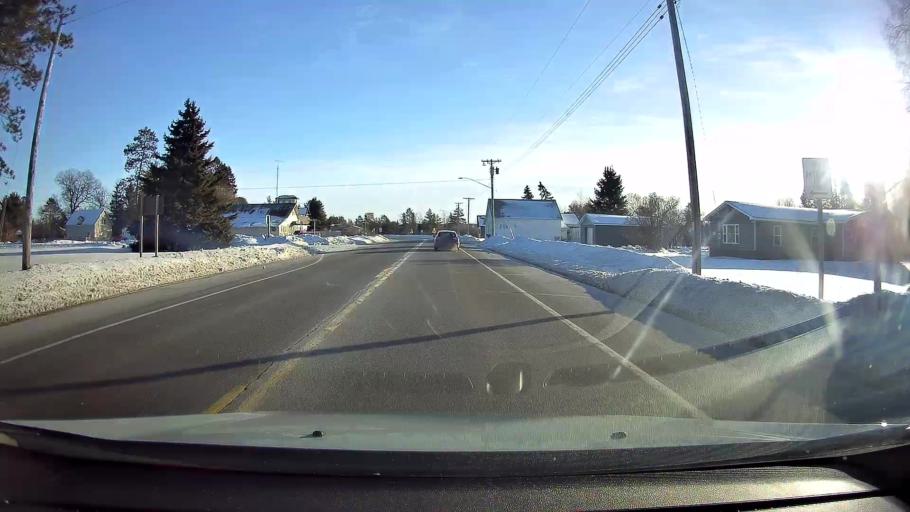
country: US
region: Wisconsin
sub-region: Washburn County
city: Spooner
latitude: 45.9104
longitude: -91.7632
